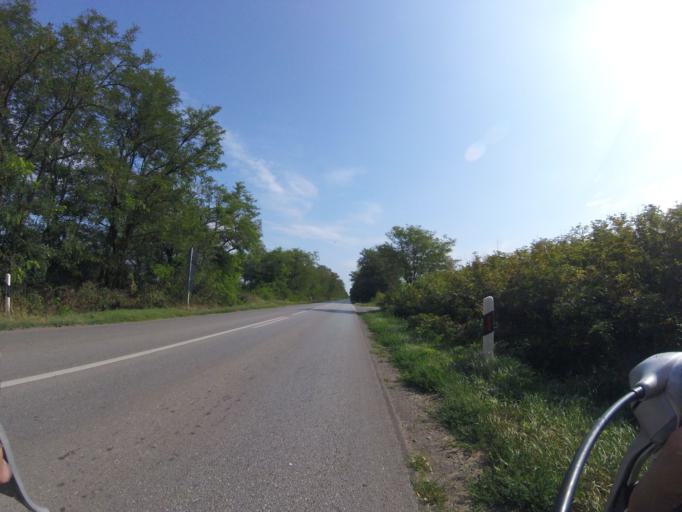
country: HU
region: Szabolcs-Szatmar-Bereg
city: Kemecse
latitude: 48.0507
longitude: 21.7710
